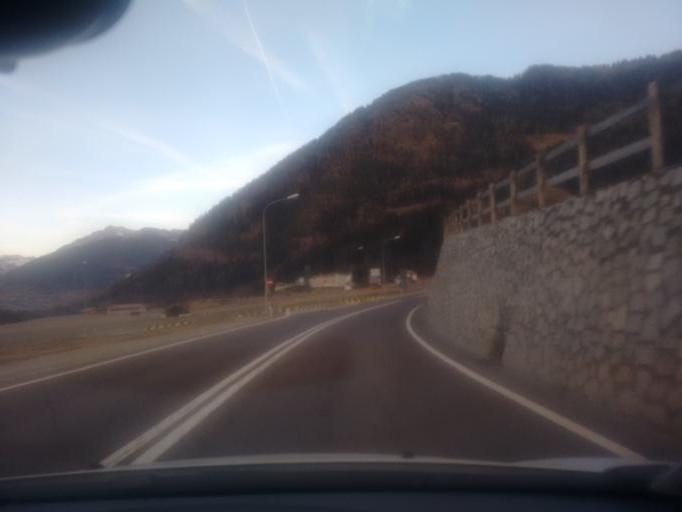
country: IT
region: Trentino-Alto Adige
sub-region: Bolzano
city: Campo di Trens
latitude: 46.8725
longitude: 11.4827
